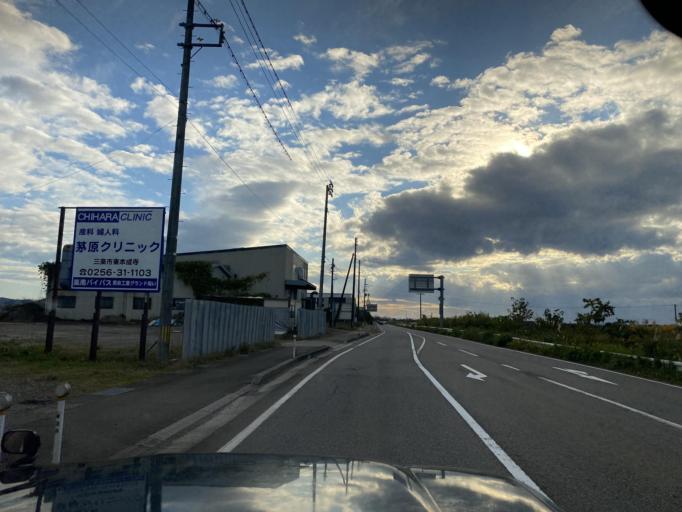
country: JP
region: Niigata
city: Kamo
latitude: 37.6793
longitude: 139.0177
